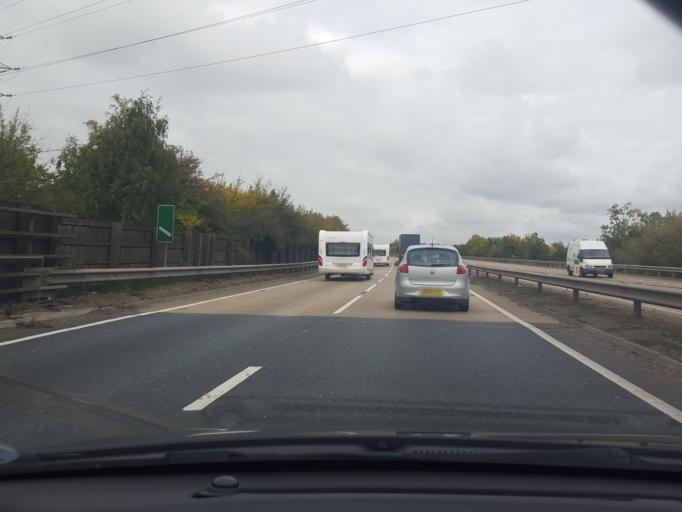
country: GB
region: England
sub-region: Suffolk
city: Bramford
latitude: 52.0604
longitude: 1.1064
